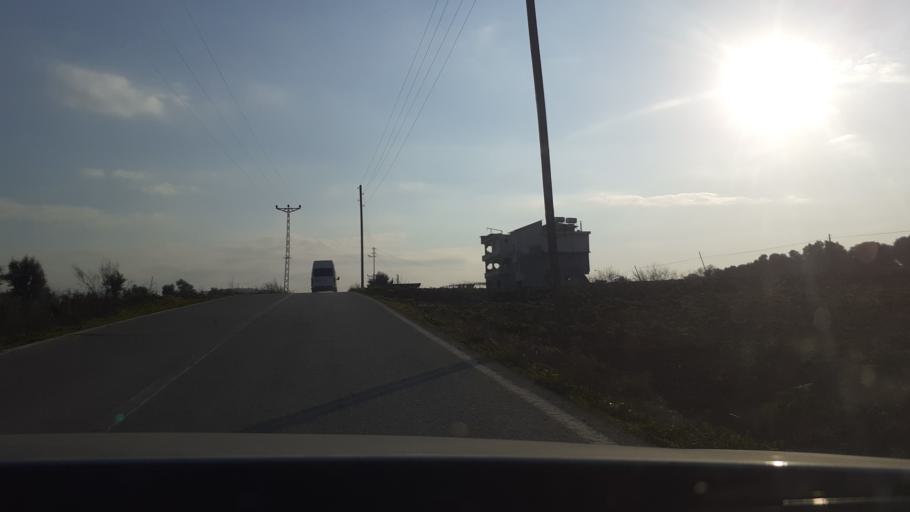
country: TR
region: Hatay
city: Boynuyogun
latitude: 36.1360
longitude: 36.3132
